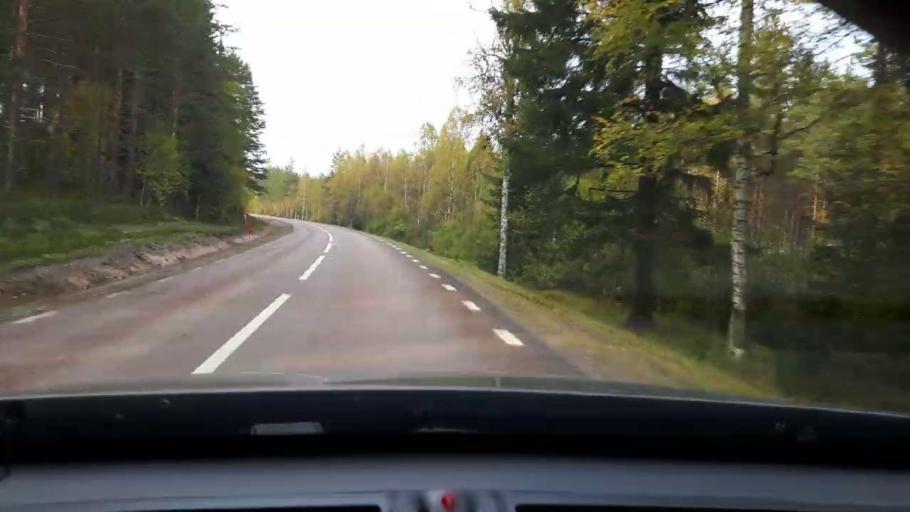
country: SE
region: Dalarna
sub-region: Gagnefs Kommun
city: Mockfjard
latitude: 60.3351
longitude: 14.9230
